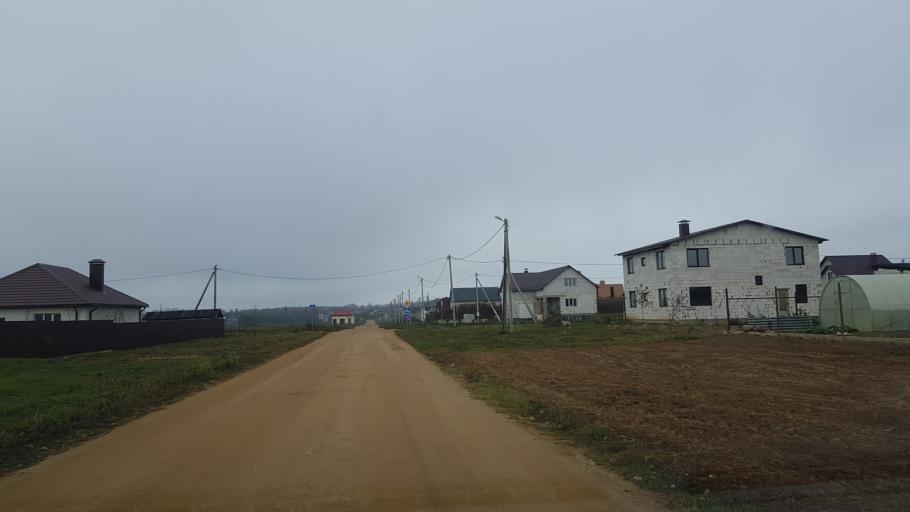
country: BY
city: Fanipol
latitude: 53.7275
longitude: 27.3252
